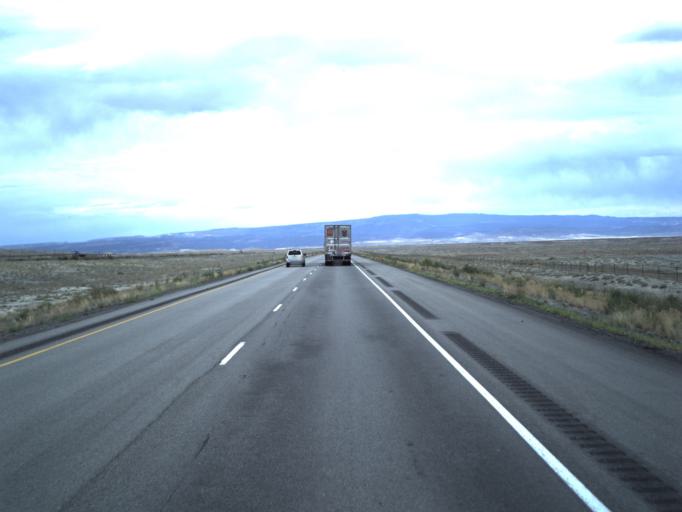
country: US
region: Utah
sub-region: Grand County
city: Moab
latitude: 38.9341
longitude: -109.4565
